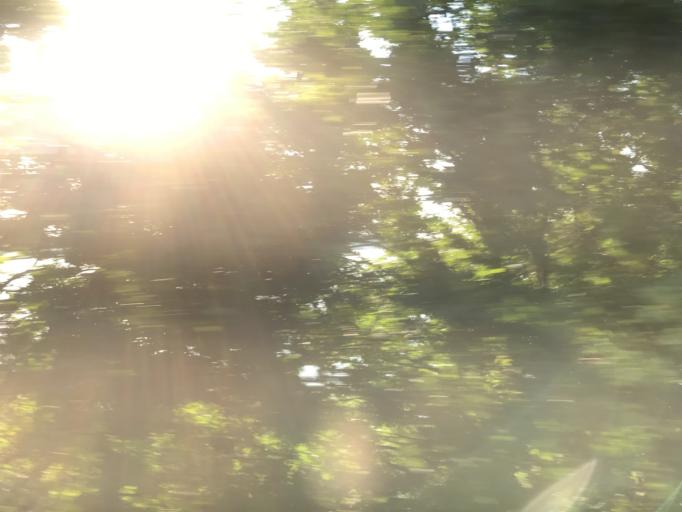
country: CZ
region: Jihocesky
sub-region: Okres Jindrichuv Hradec
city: Trebon
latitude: 49.0370
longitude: 14.7512
